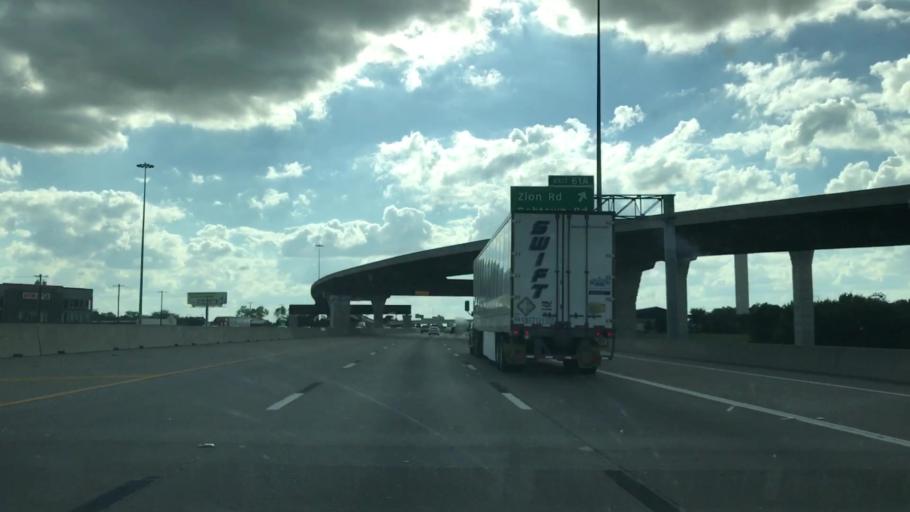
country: US
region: Texas
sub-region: Dallas County
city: Rowlett
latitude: 32.8561
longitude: -96.5562
